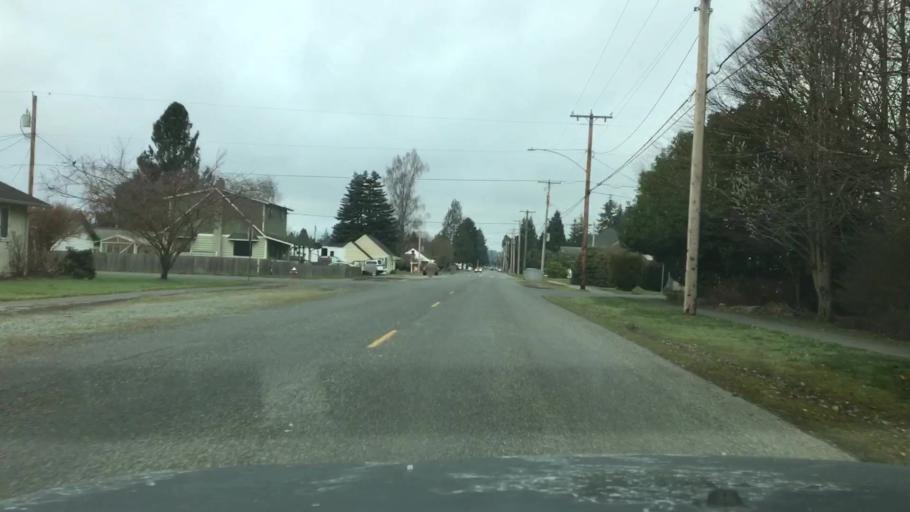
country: US
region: Washington
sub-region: Skagit County
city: Sedro-Woolley
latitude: 48.4958
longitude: -122.2260
